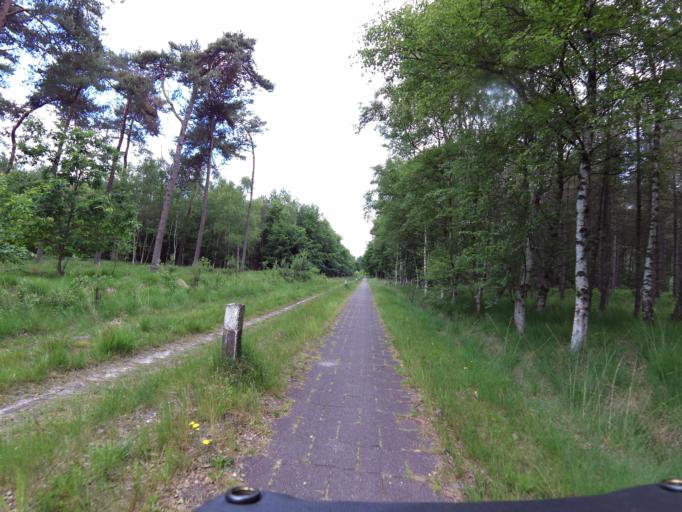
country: NL
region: North Brabant
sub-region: Gemeente Baarle-Nassau
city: Baarle-Nassau
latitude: 51.5025
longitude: 4.9175
